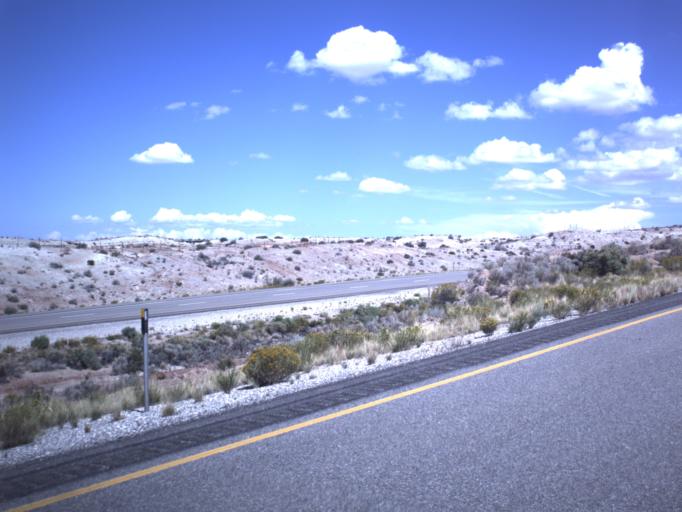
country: US
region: Utah
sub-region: Emery County
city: Ferron
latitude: 38.8472
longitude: -111.0159
